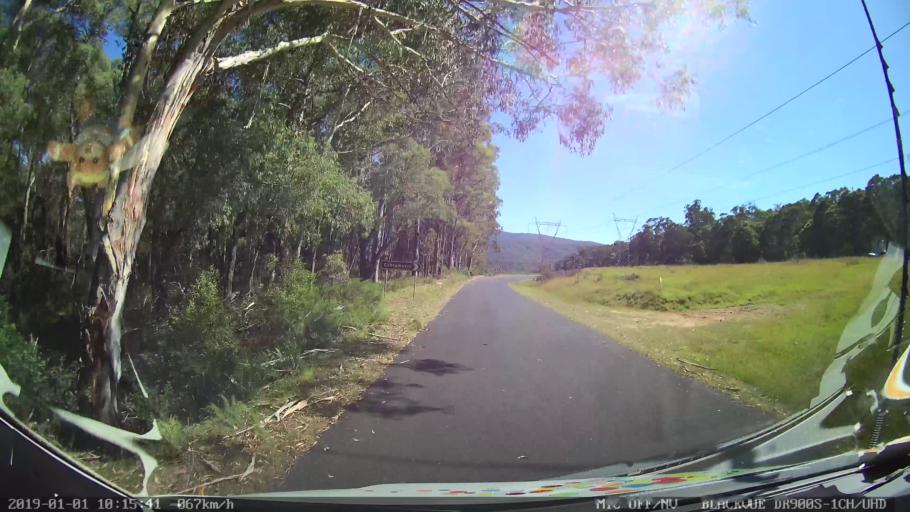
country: AU
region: New South Wales
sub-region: Snowy River
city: Jindabyne
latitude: -36.0992
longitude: 148.1621
